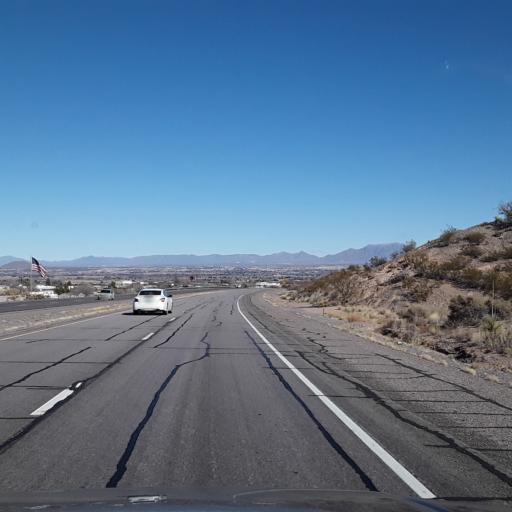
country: US
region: New Mexico
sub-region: Dona Ana County
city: Mesilla
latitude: 32.2897
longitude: -106.8719
